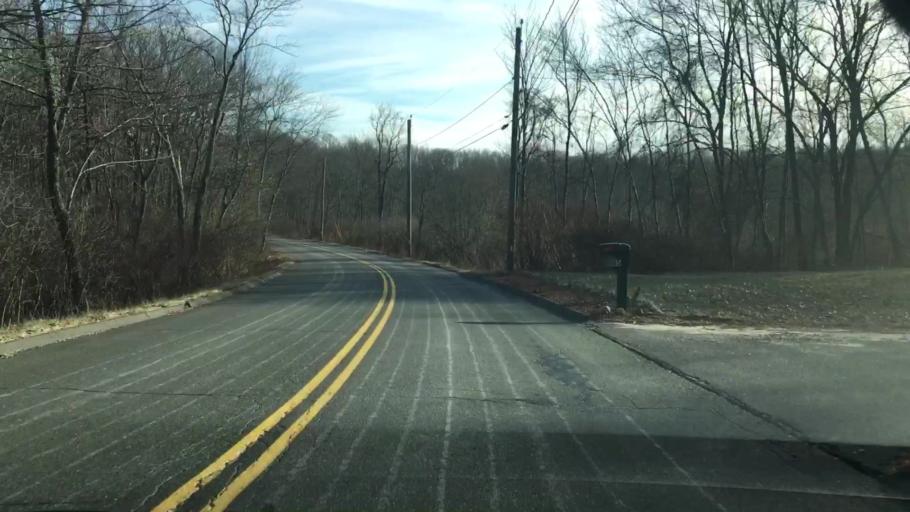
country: US
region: Connecticut
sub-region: New Haven County
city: Prospect
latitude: 41.5342
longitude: -72.9664
